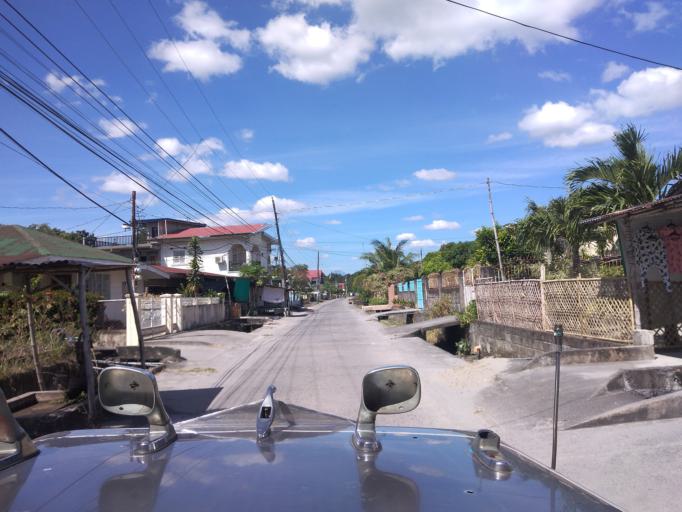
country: PH
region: Central Luzon
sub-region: Province of Pampanga
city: Santa Rita
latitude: 15.0028
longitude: 120.6059
